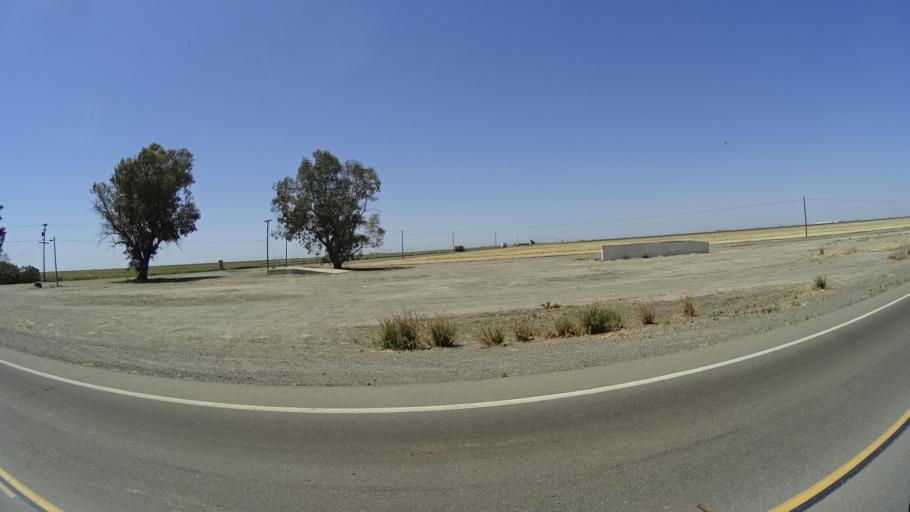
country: US
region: California
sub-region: Kings County
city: Corcoran
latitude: 36.1387
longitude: -119.6449
